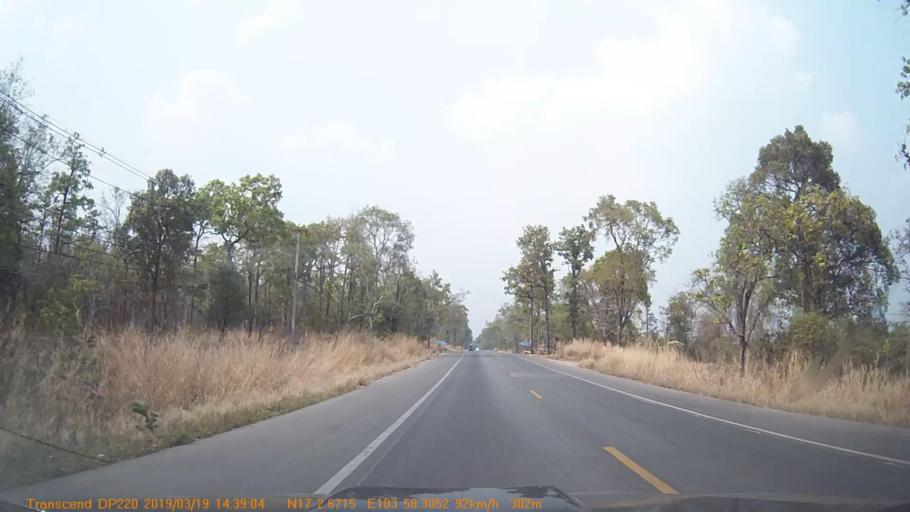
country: TH
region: Sakon Nakhon
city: Phu Phan
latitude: 17.0449
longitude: 103.9717
